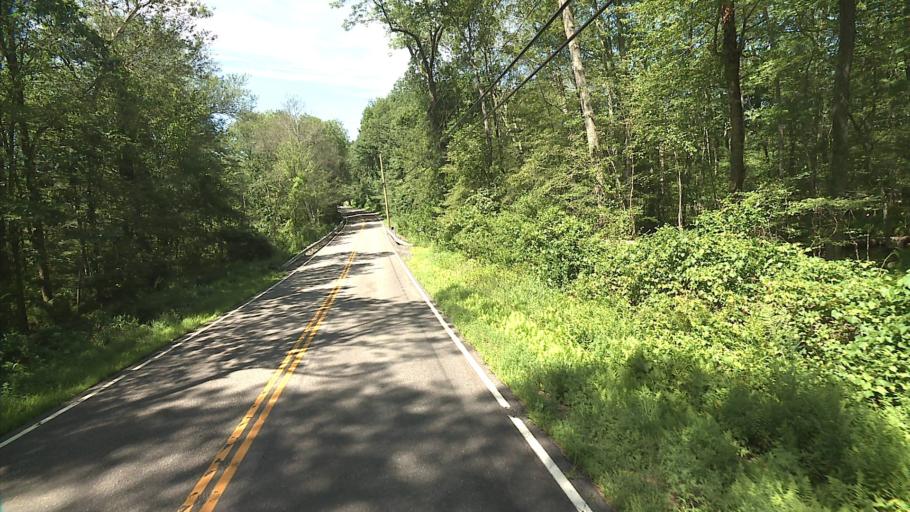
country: US
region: Connecticut
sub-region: Windham County
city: South Woodstock
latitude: 41.8992
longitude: -72.0122
